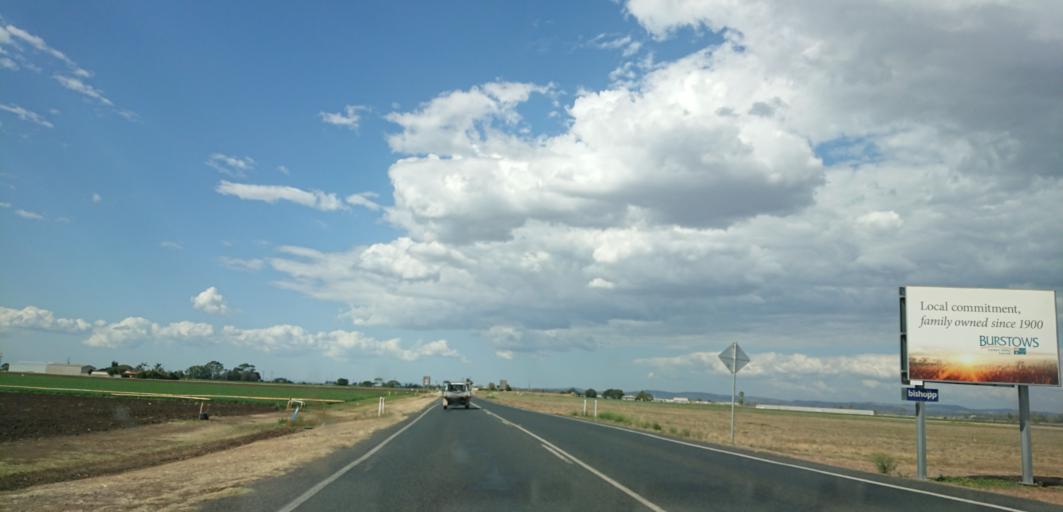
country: AU
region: Queensland
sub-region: Lockyer Valley
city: Gatton
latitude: -27.5555
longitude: 152.2962
